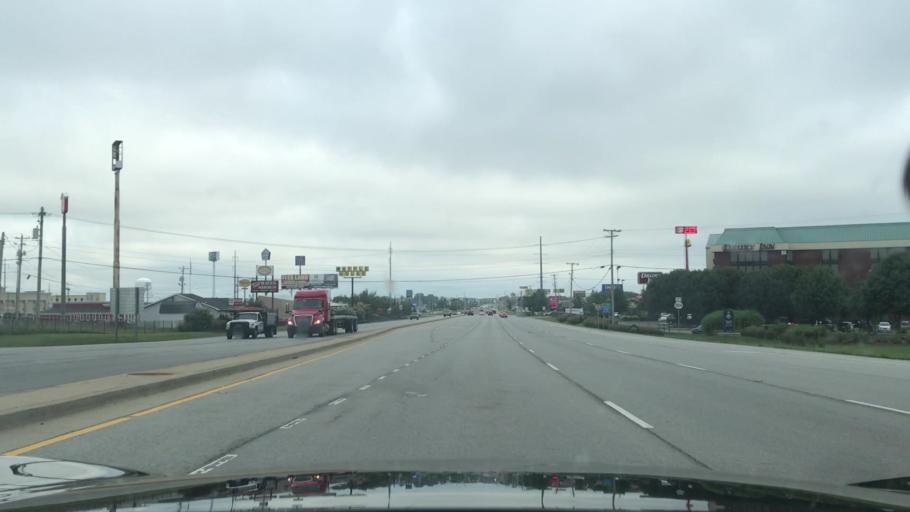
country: US
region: Kentucky
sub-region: Warren County
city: Plano
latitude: 36.9370
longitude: -86.4194
